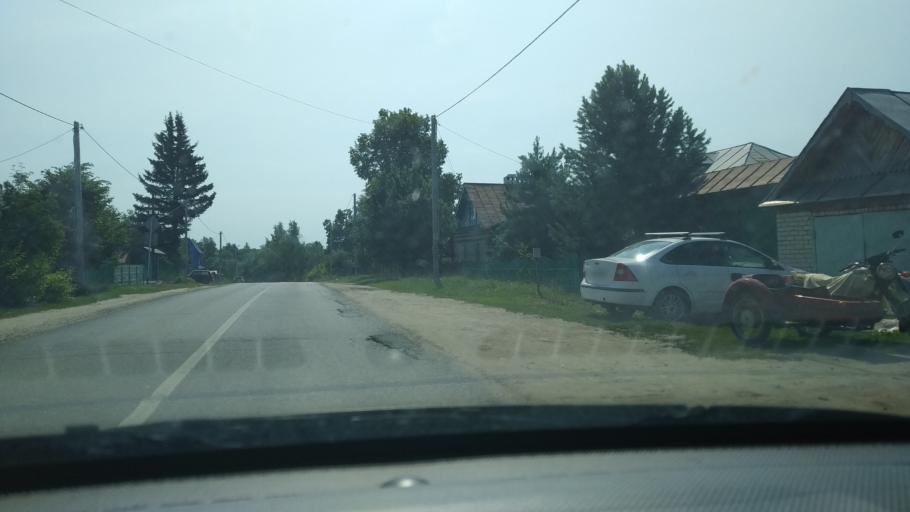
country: RU
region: Tatarstan
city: Osinovo
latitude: 55.9828
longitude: 48.7952
